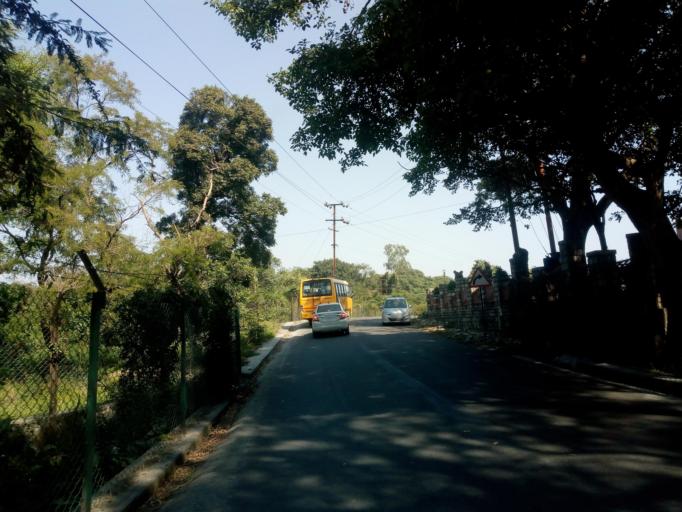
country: IN
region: Himachal Pradesh
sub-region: Sirmaur
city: Paonta Sahib
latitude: 30.4394
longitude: 77.6684
